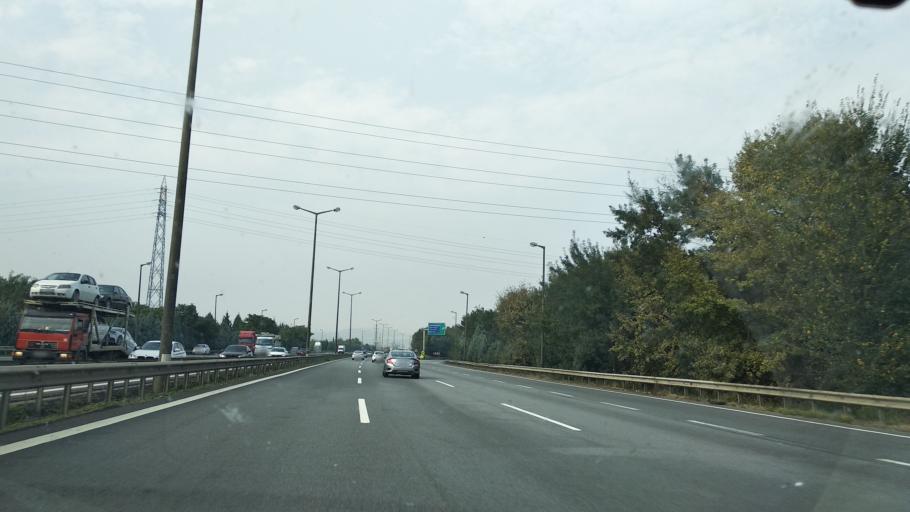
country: TR
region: Kocaeli
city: Kosekoy
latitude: 40.7438
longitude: 30.0430
